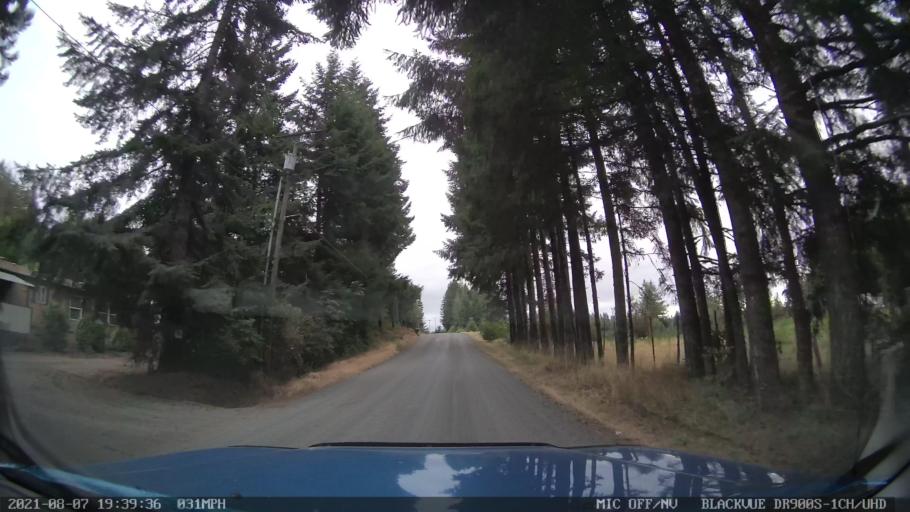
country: US
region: Oregon
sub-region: Marion County
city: Silverton
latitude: 44.9348
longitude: -122.6569
